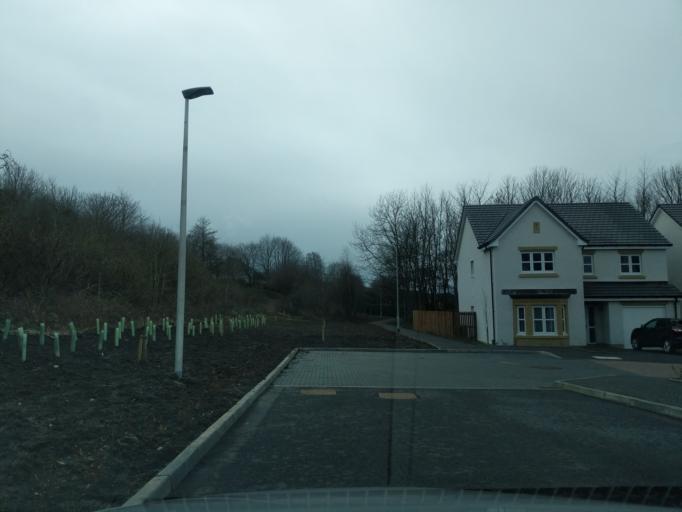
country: GB
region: Scotland
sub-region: Edinburgh
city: Currie
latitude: 55.8997
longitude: -3.3172
